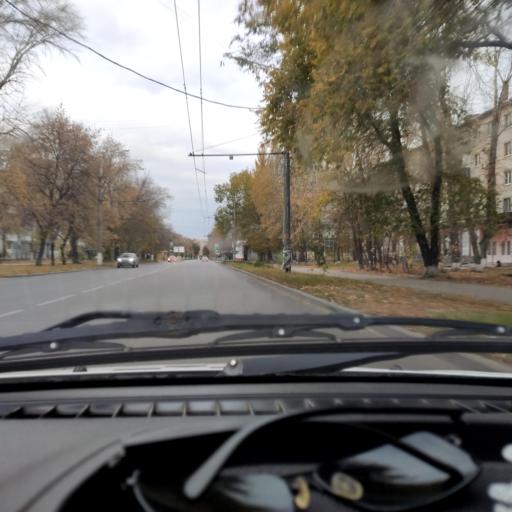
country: RU
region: Samara
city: Tol'yatti
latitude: 53.5108
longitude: 49.4304
